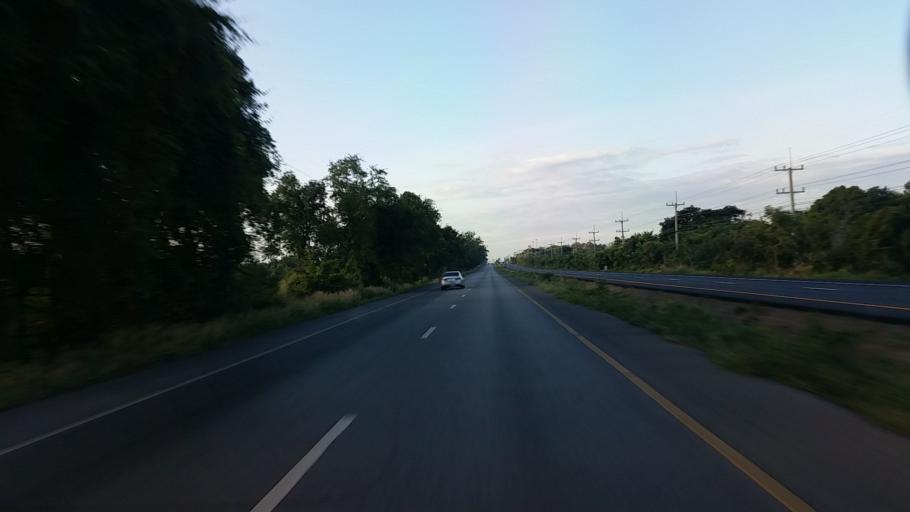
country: TH
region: Lop Buri
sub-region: Amphoe Tha Luang
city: Tha Luang
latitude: 15.1019
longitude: 101.0206
